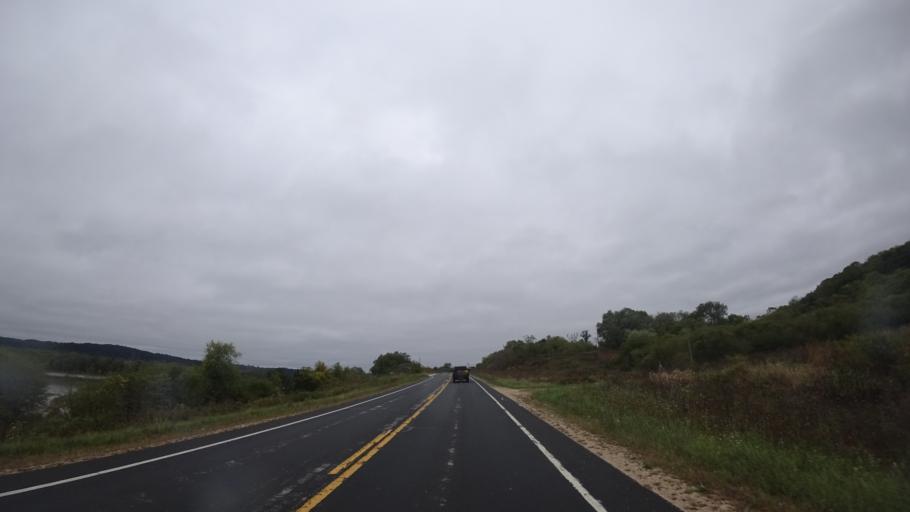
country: US
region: Wisconsin
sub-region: Grant County
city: Boscobel
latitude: 43.1150
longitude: -90.7921
